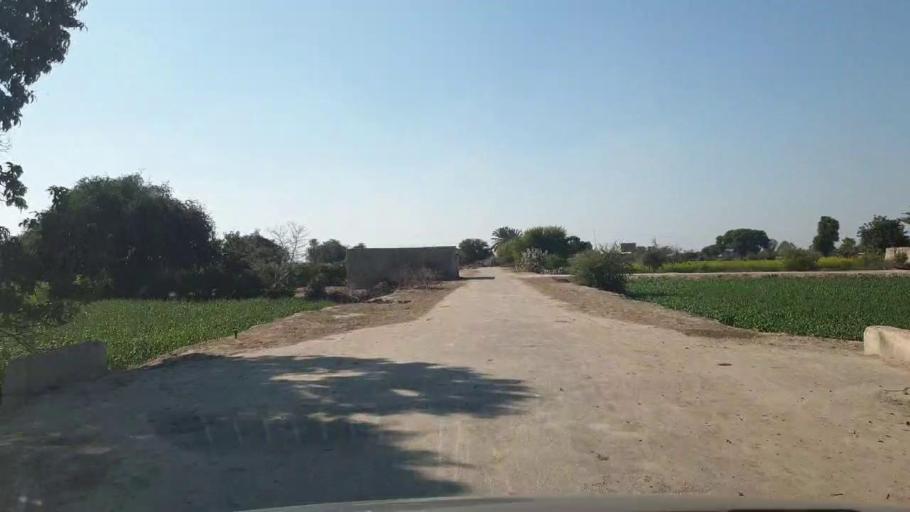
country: PK
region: Sindh
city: Shahpur Chakar
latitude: 26.1035
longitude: 68.6455
